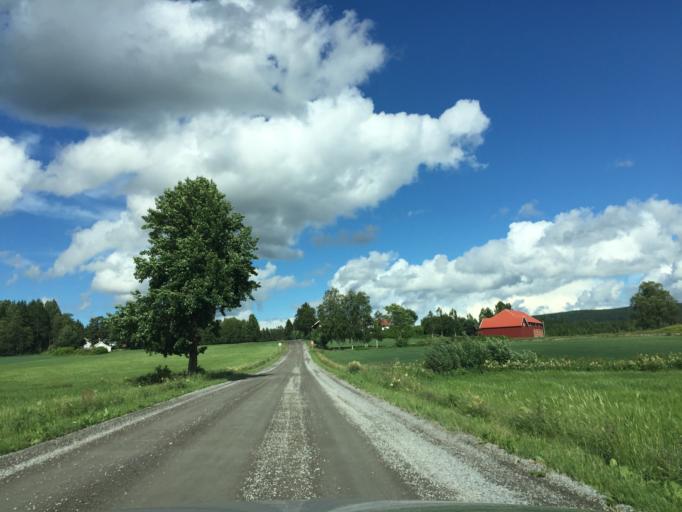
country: NO
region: Hedmark
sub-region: Kongsvinger
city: Spetalen
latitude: 60.2385
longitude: 11.8297
